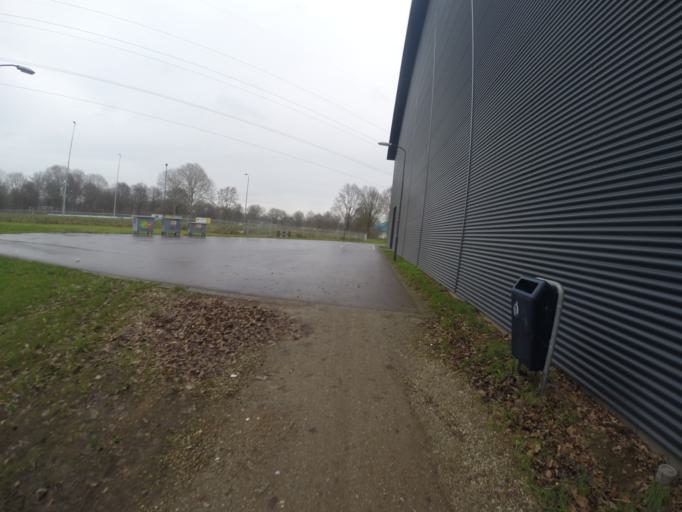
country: NL
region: Gelderland
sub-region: Gemeente Doetinchem
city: Doetinchem
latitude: 51.9642
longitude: 6.2712
